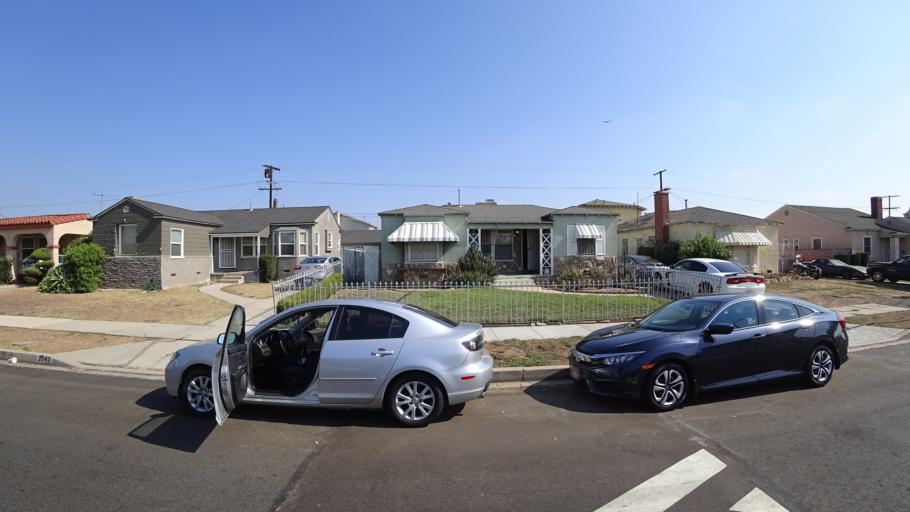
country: US
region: California
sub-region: Los Angeles County
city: Westmont
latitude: 33.9512
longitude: -118.3150
